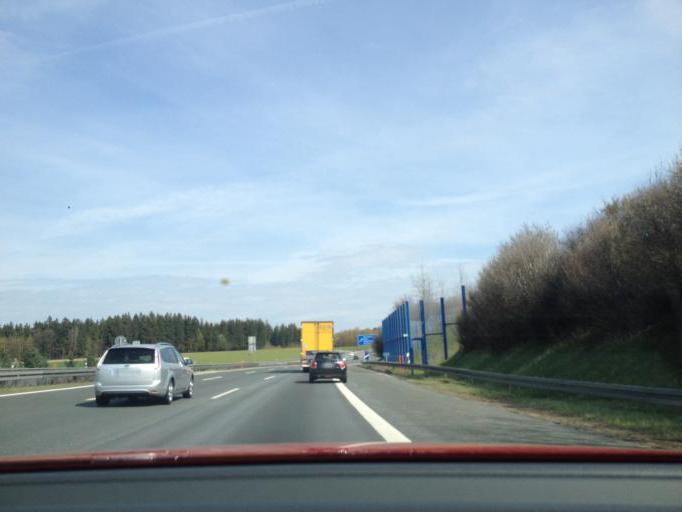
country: DE
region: Bavaria
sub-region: Upper Franconia
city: Munchberg
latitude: 50.1642
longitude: 11.7461
